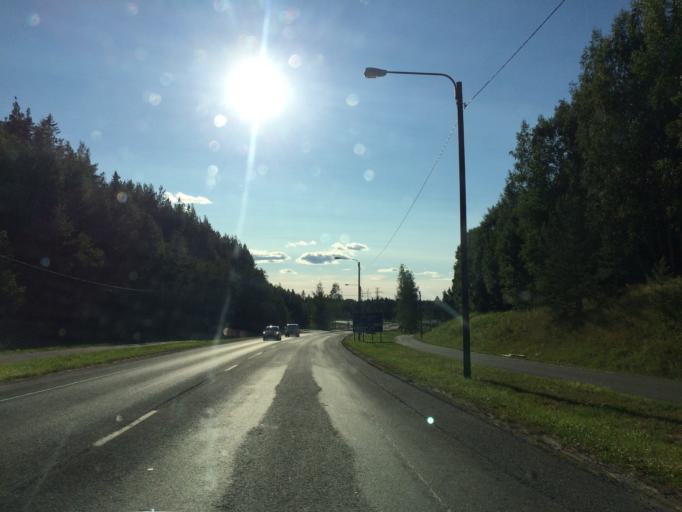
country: FI
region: Haeme
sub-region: Haemeenlinna
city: Haemeenlinna
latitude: 60.9828
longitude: 24.5127
